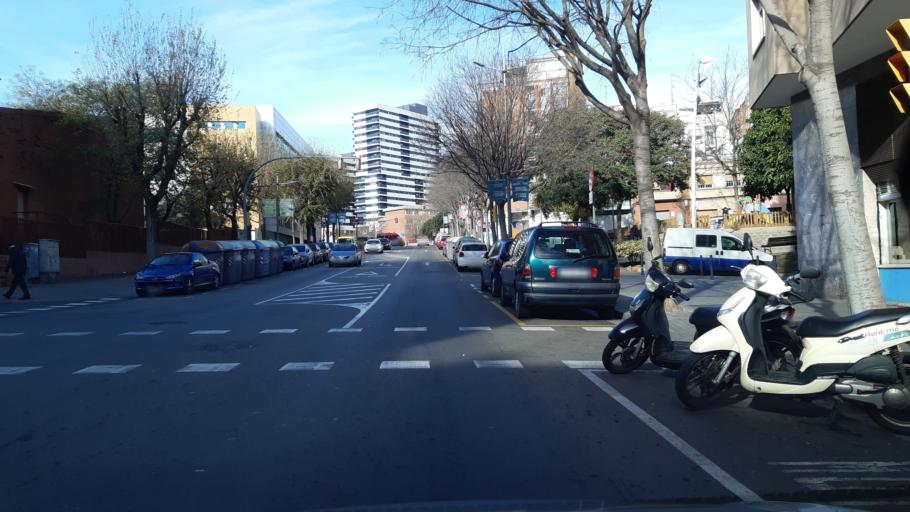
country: ES
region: Catalonia
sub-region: Provincia de Barcelona
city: L'Hospitalet de Llobregat
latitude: 41.3730
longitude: 2.1129
